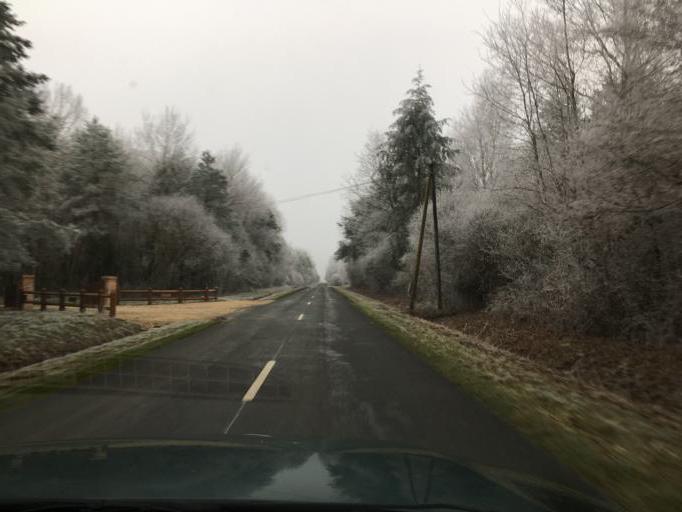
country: FR
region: Centre
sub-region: Departement du Loir-et-Cher
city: Chaumont-sur-Tharonne
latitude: 47.6187
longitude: 1.8275
